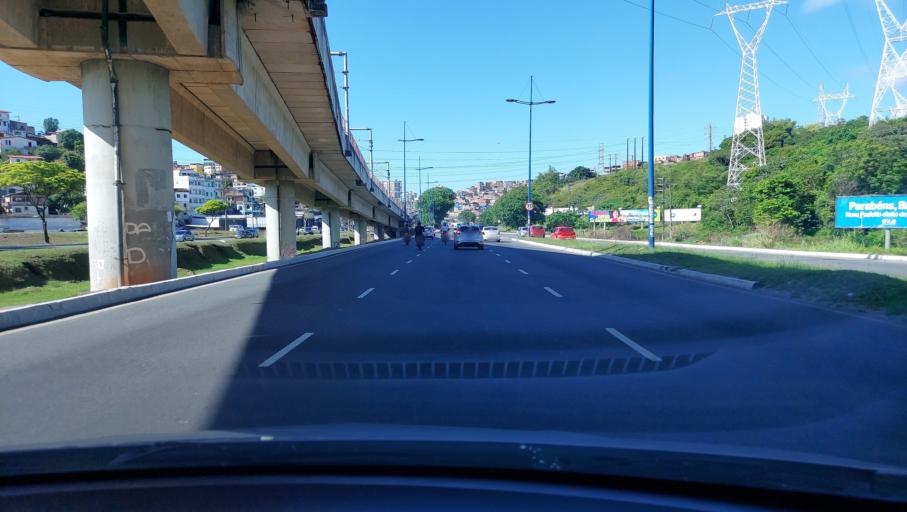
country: BR
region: Bahia
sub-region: Salvador
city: Salvador
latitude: -12.9759
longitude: -38.4782
